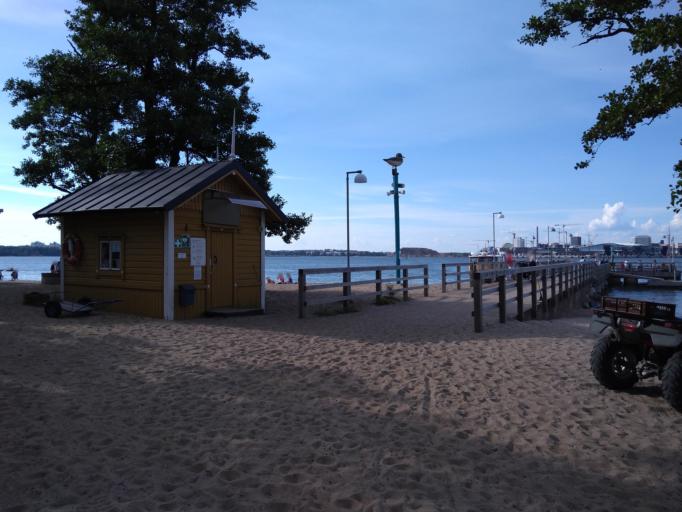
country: FI
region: Uusimaa
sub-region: Helsinki
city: Helsinki
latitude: 60.1400
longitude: 24.9163
